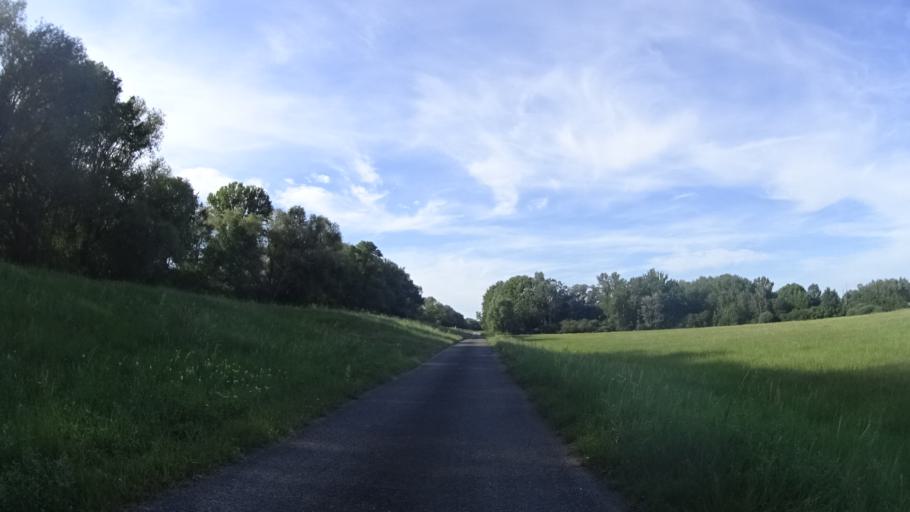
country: AT
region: Lower Austria
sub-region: Politischer Bezirk Ganserndorf
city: Drosing
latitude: 48.5511
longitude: 16.9622
